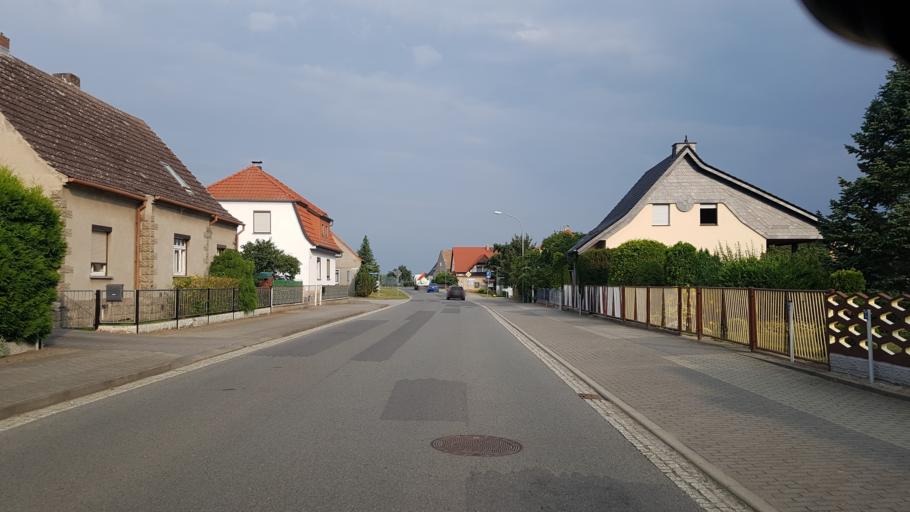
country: DE
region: Brandenburg
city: Grossthiemig
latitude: 51.3843
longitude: 13.6705
